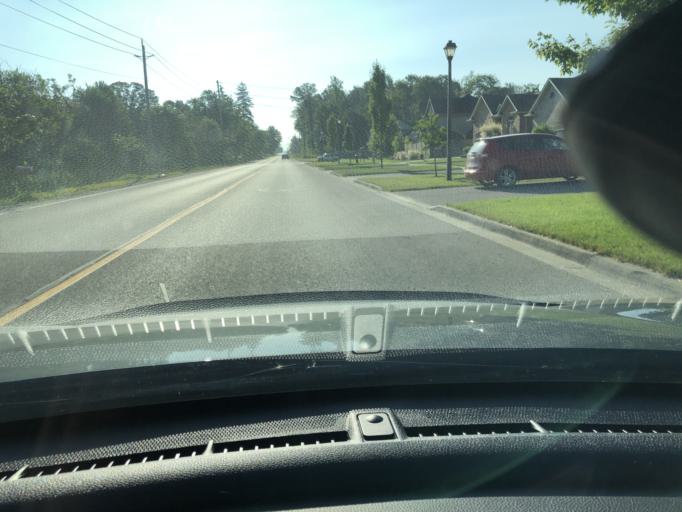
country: CA
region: Ontario
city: Stratford
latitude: 43.3893
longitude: -80.9599
